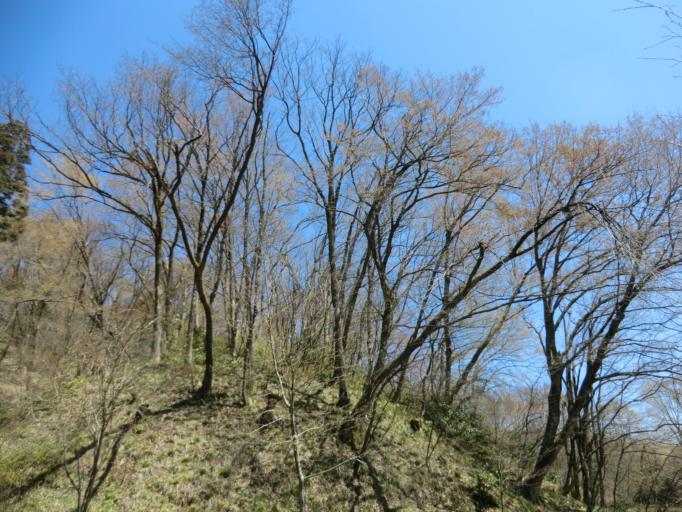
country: JP
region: Niigata
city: Nagaoka
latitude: 37.4652
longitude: 138.7437
